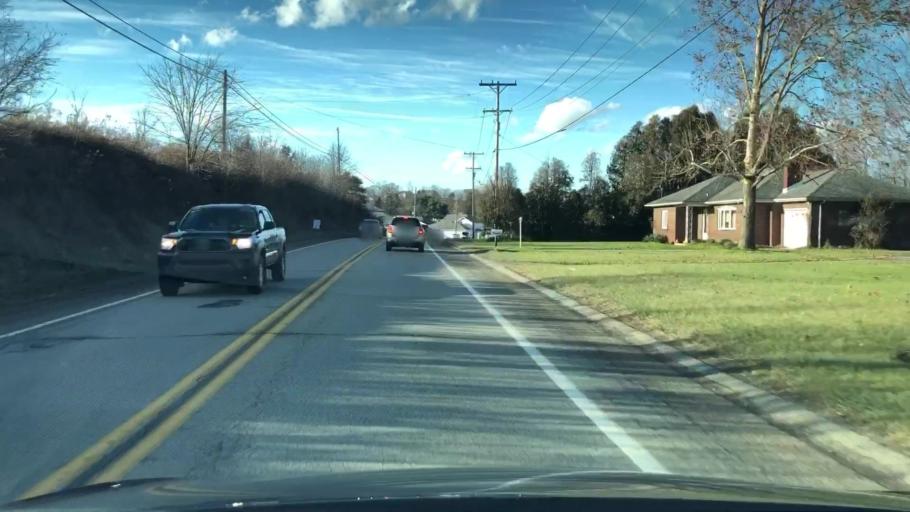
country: US
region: Pennsylvania
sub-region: Butler County
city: Saxonburg
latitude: 40.7157
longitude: -79.7516
